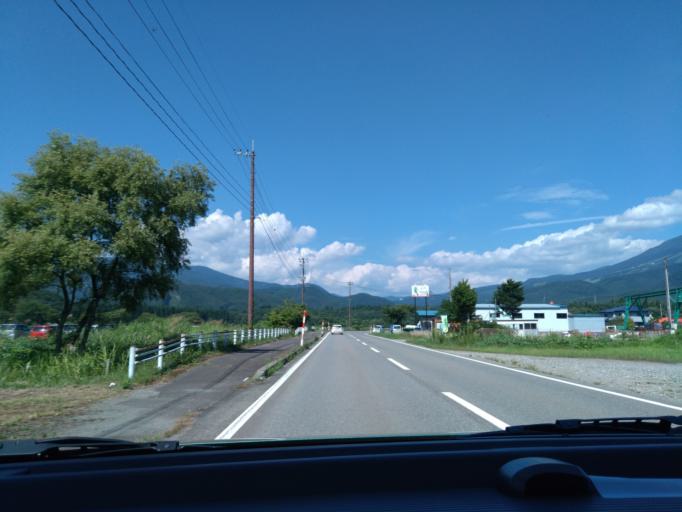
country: JP
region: Akita
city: Kakunodatemachi
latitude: 39.7393
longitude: 140.7111
